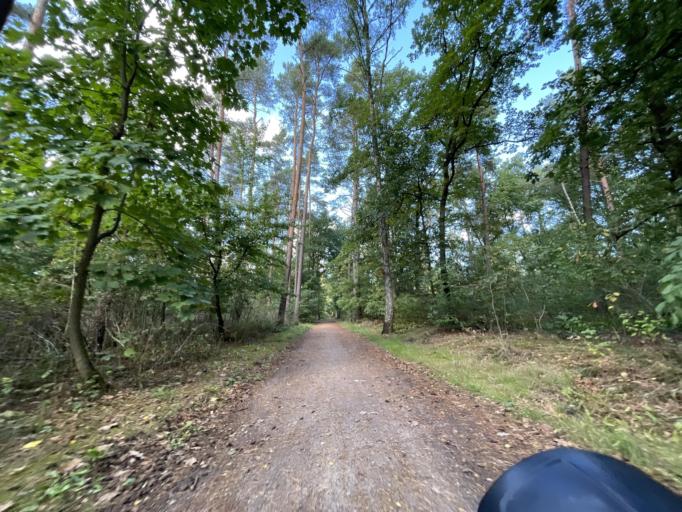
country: DE
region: Lower Saxony
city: Lueneburg
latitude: 53.2315
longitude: 10.4283
